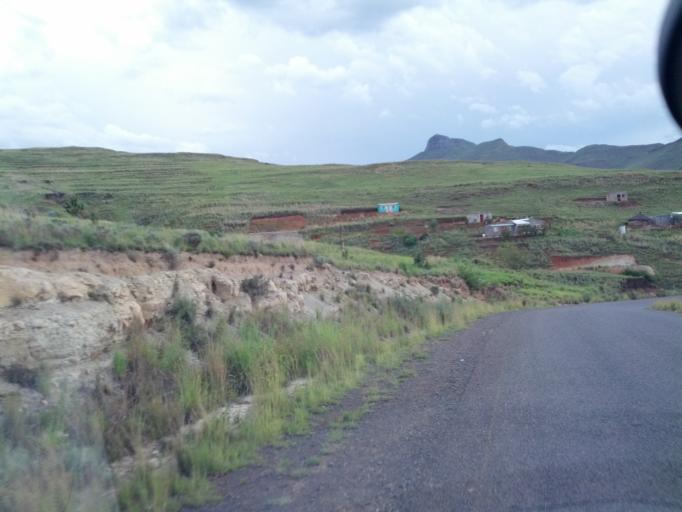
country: LS
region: Qacha's Nek
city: Qacha's Nek
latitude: -30.0726
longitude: 28.5875
